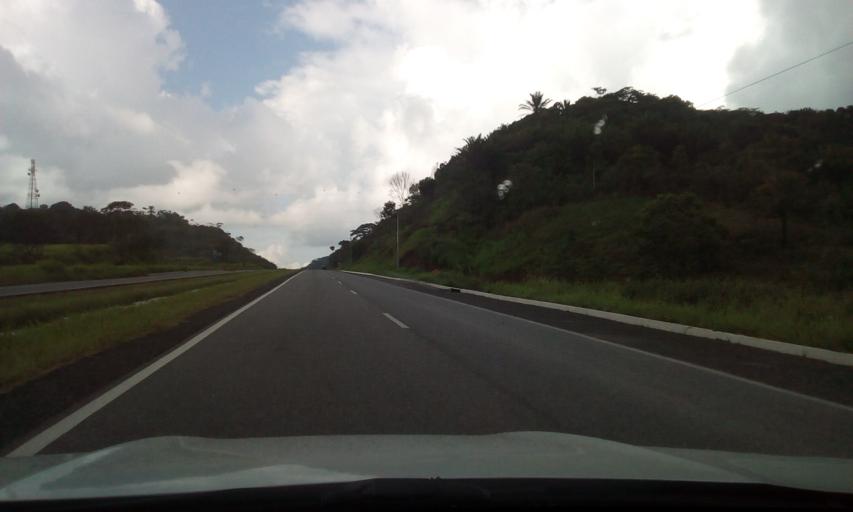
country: BR
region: Pernambuco
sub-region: Cabo De Santo Agostinho
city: Cabo
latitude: -8.2613
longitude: -35.0475
